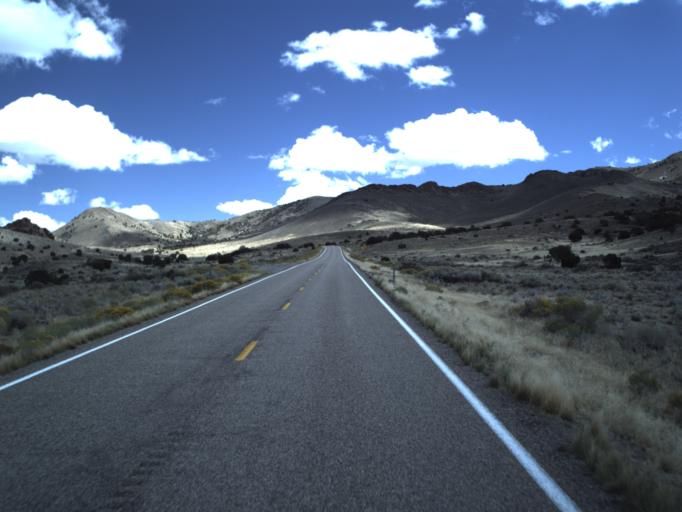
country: US
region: Utah
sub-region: Beaver County
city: Milford
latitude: 38.4347
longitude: -113.2931
